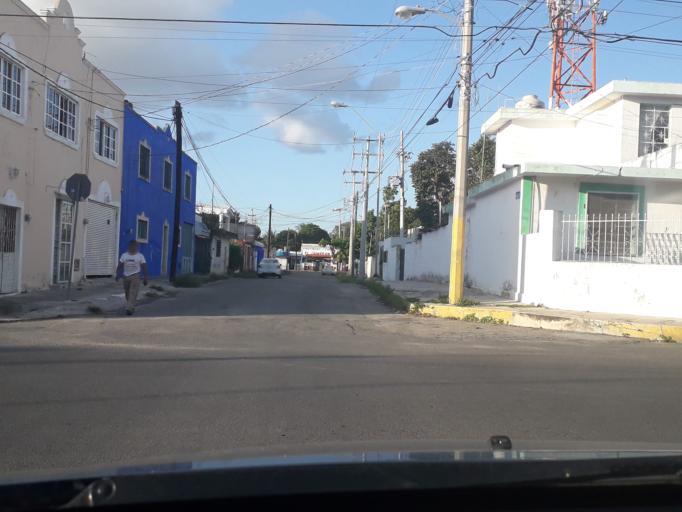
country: MX
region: Yucatan
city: Merida
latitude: 20.9712
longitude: -89.6455
